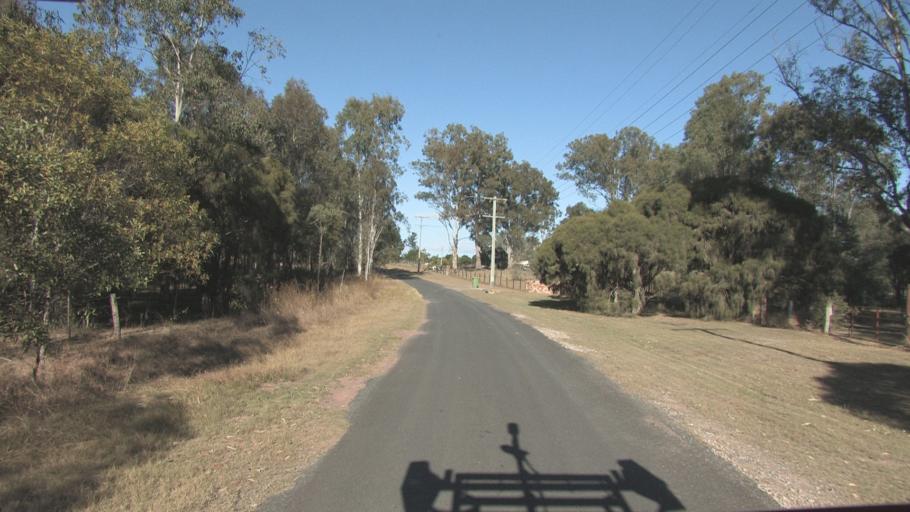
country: AU
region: Queensland
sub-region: Logan
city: Cedar Vale
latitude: -27.8422
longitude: 152.9971
